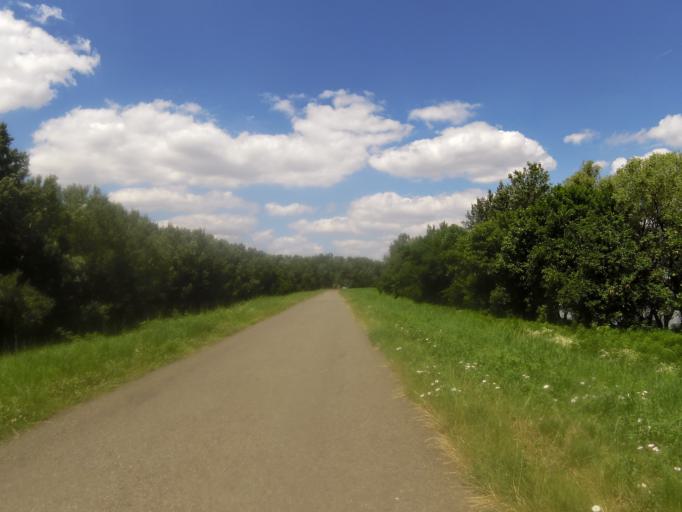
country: HU
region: Heves
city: Tiszanana
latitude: 47.5481
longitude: 20.6062
